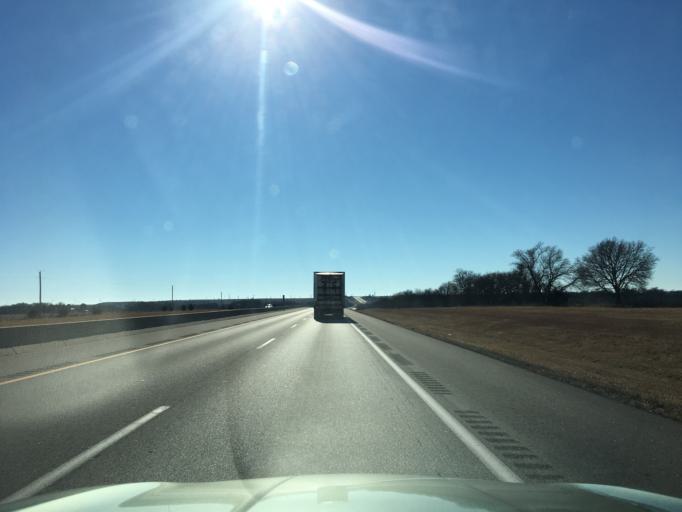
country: US
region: Kansas
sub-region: Sumner County
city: Wellington
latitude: 37.2255
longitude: -97.3389
